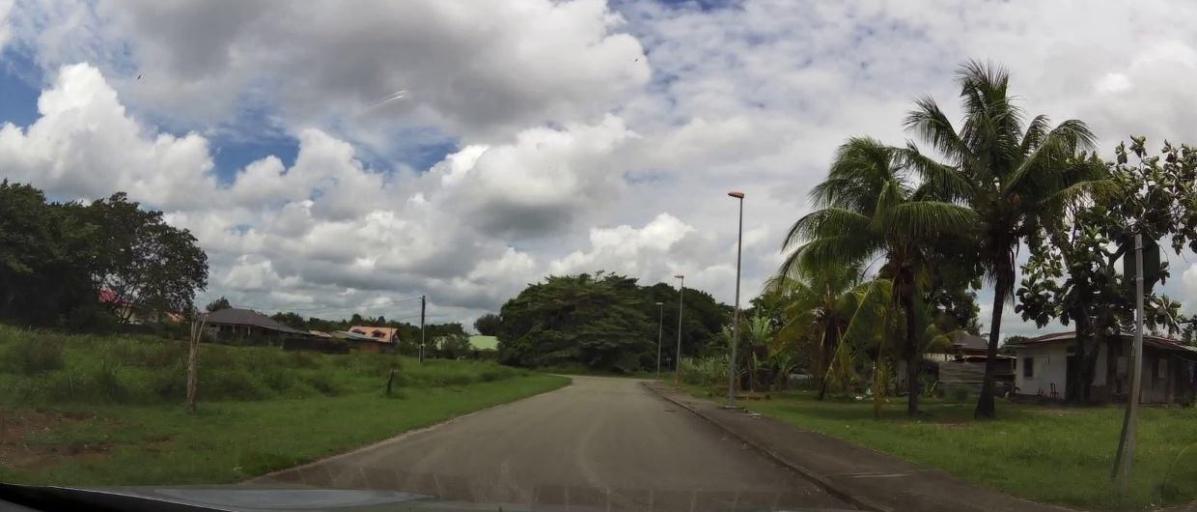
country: GF
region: Guyane
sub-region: Guyane
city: Sinnamary
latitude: 5.3731
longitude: -52.9554
